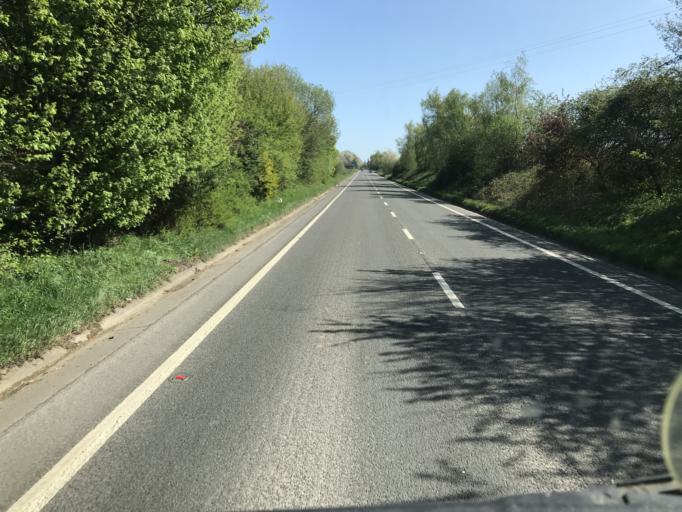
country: GB
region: England
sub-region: Cheshire East
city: Willaston
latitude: 53.0738
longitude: -2.5003
